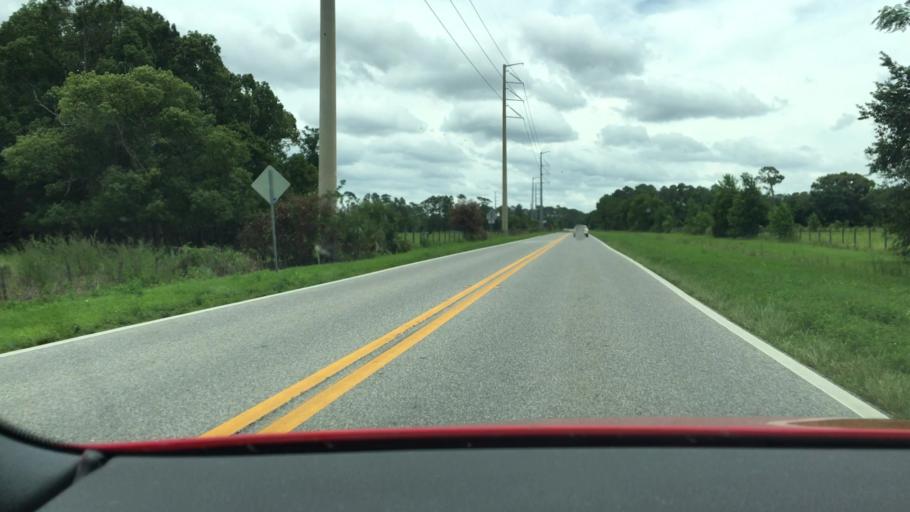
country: US
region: Florida
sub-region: Lake County
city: Eustis
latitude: 28.8734
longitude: -81.6667
